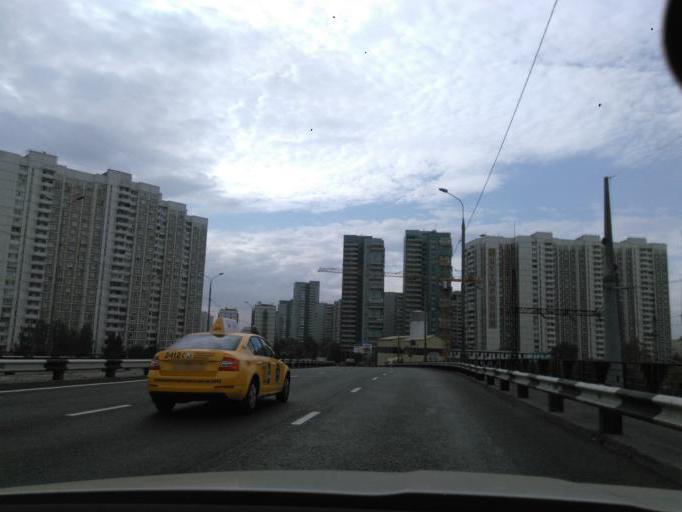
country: RU
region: Moscow
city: Novovladykino
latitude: 55.8326
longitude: 37.5775
